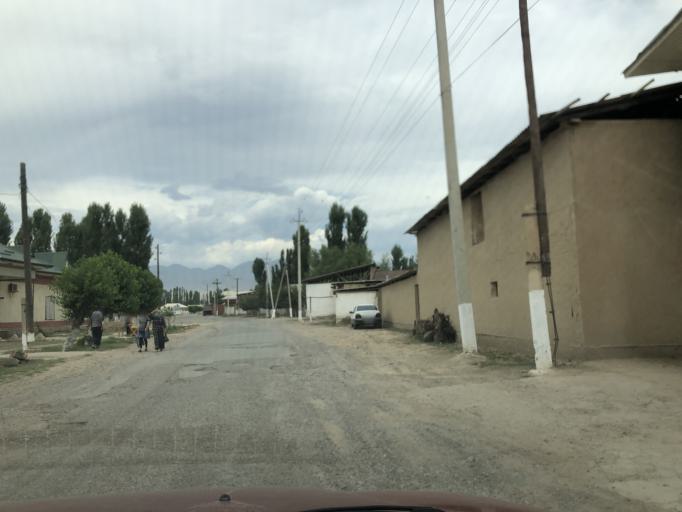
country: UZ
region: Namangan
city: Pop Shahri
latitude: 41.0107
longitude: 71.0885
